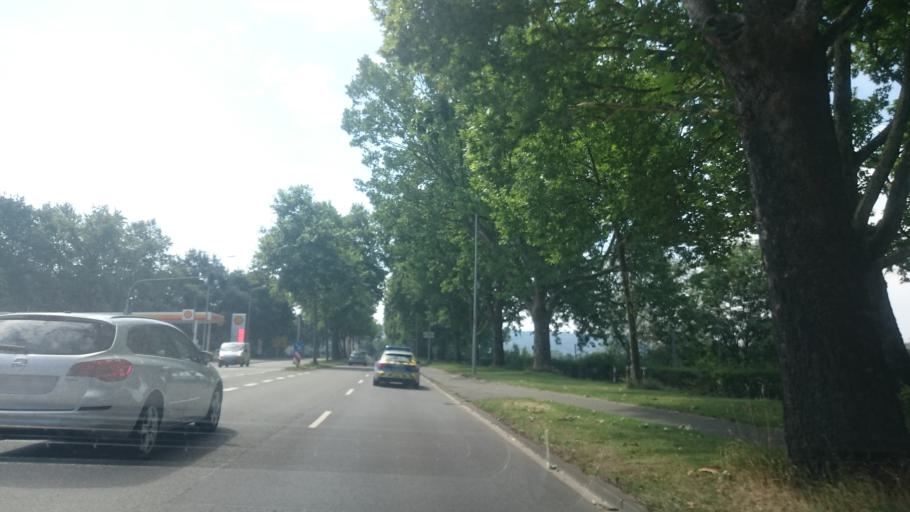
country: DE
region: Rheinland-Pfalz
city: Trier
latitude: 49.7467
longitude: 6.6278
